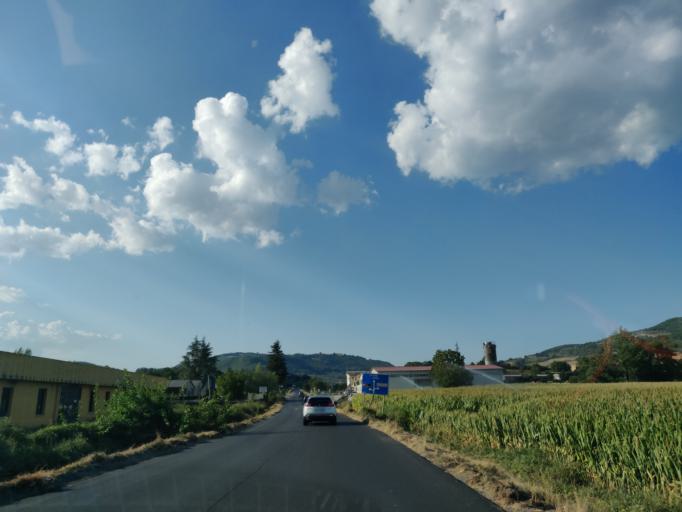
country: IT
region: Latium
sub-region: Provincia di Viterbo
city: Acquapendente
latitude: 42.7657
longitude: 11.8563
